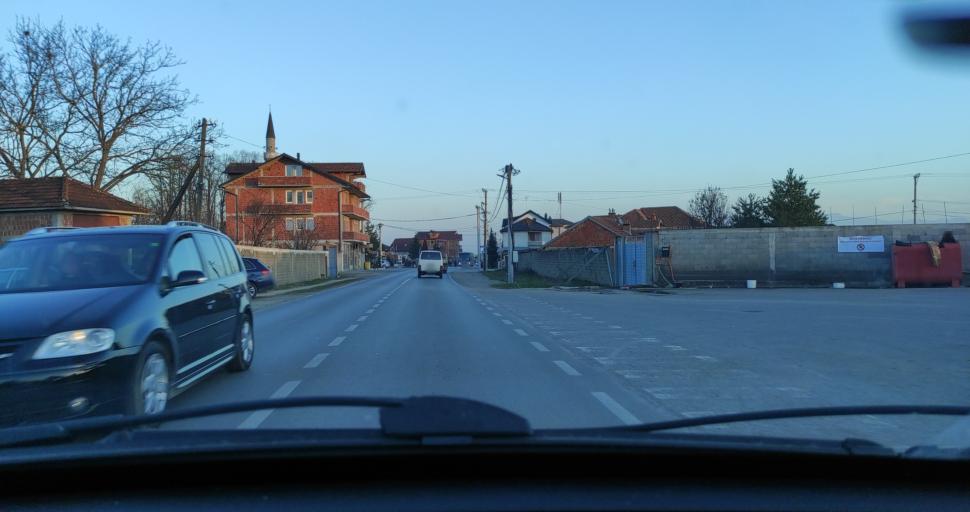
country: XK
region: Gjakova
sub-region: Komuna e Gjakoves
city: Gjakove
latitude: 42.4315
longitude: 20.3818
